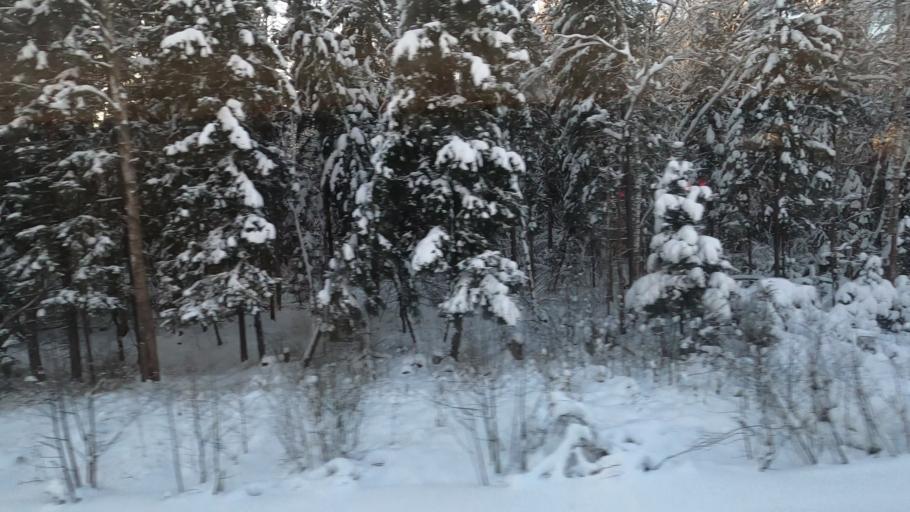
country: RU
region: Moskovskaya
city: Novo-Nikol'skoye
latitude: 56.5967
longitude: 37.5665
